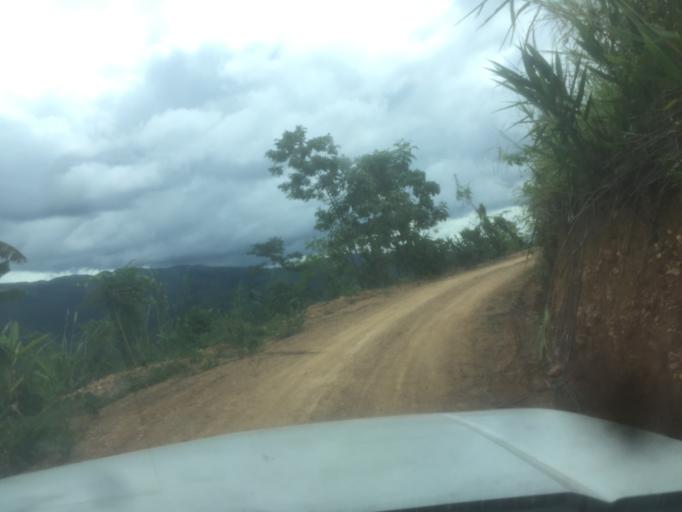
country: LA
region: Phongsali
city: Khoa
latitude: 20.9257
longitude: 102.5433
